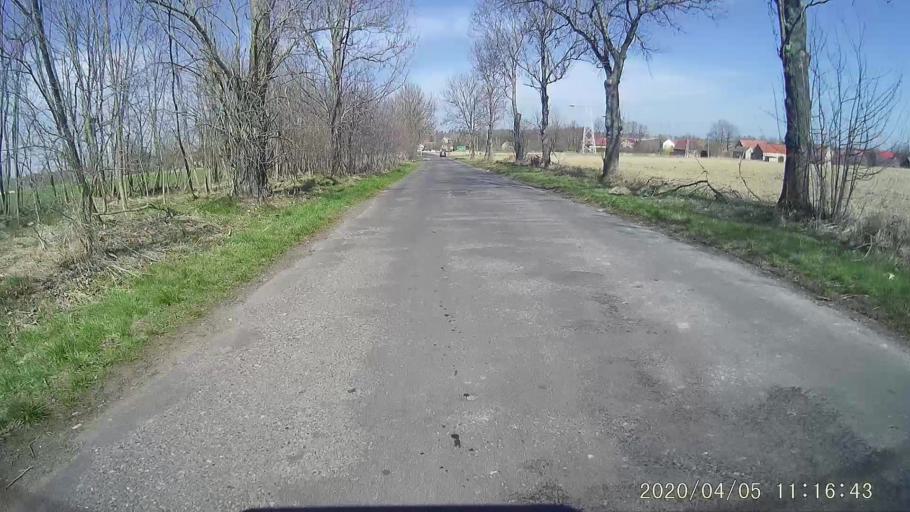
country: PL
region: Lower Silesian Voivodeship
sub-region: Powiat zgorzelecki
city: Sulikow
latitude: 51.0777
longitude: 15.1033
